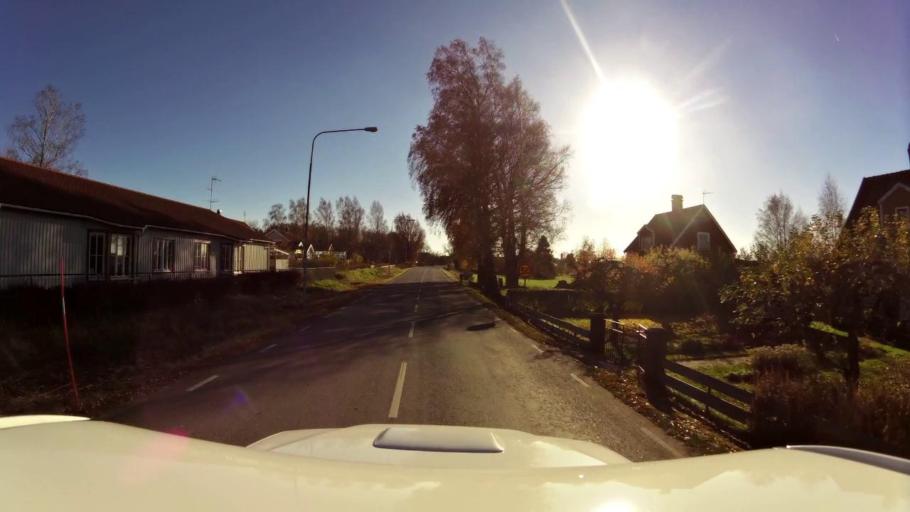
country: SE
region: OEstergoetland
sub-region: Linkopings Kommun
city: Malmslatt
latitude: 58.3614
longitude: 15.5625
